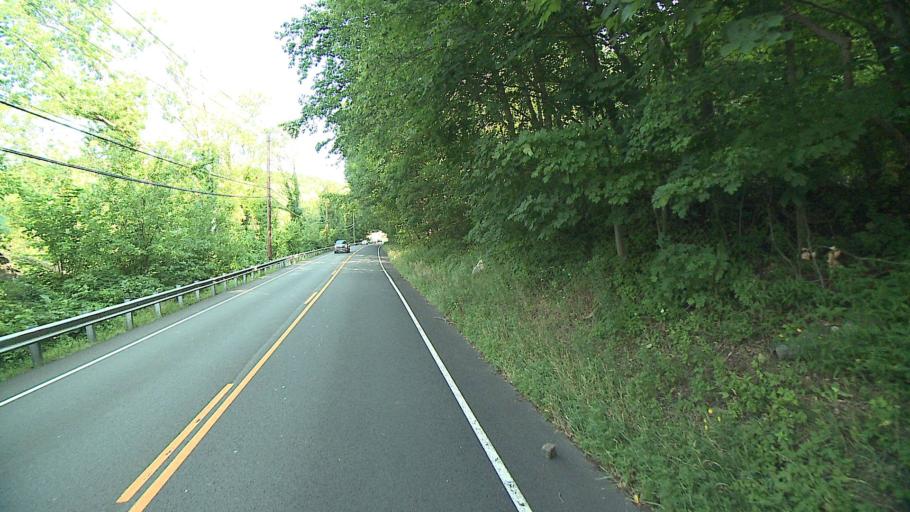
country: US
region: Connecticut
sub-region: Fairfield County
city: Ridgefield
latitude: 41.3178
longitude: -73.4745
